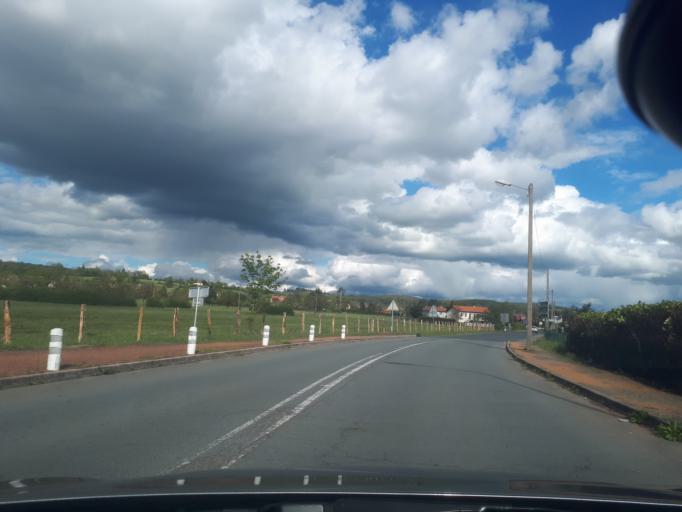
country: FR
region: Rhone-Alpes
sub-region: Departement de la Loire
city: Balbigny
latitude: 45.8177
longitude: 4.1960
